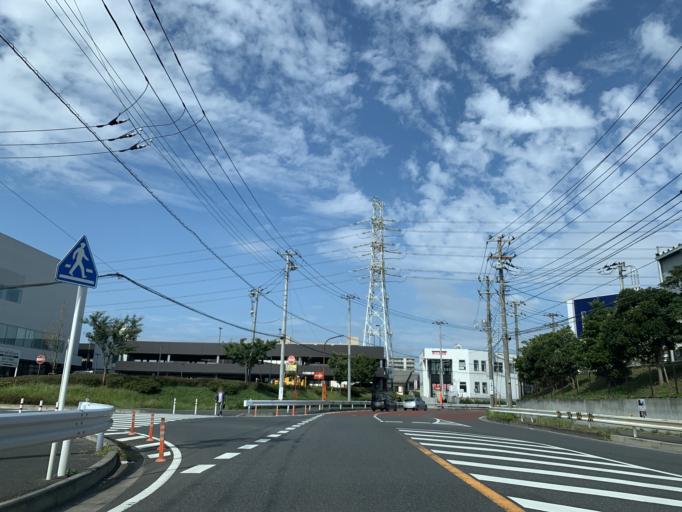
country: JP
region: Tokyo
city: Urayasu
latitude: 35.6798
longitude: 139.9323
